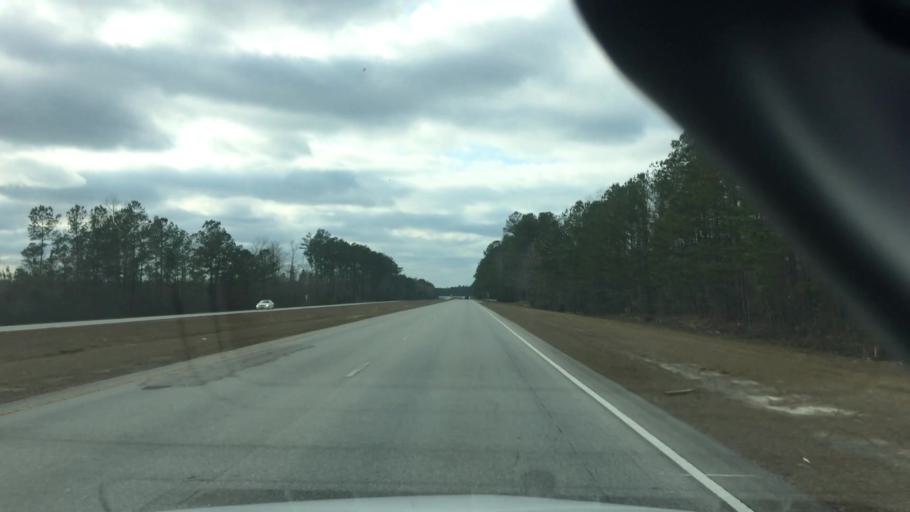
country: US
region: North Carolina
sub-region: Brunswick County
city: Bolivia
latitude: 34.0666
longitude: -78.1842
